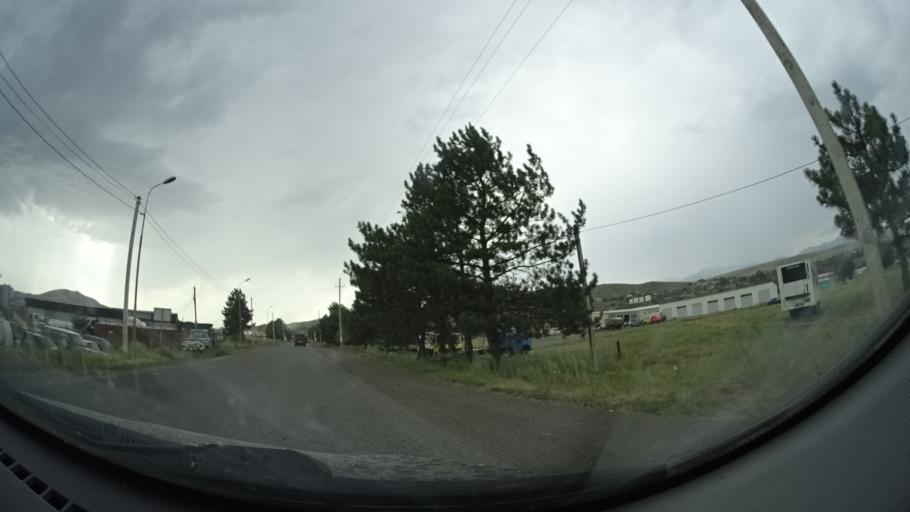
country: GE
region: Samtskhe-Javakheti
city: Akhaltsikhe
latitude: 41.6429
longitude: 43.0091
